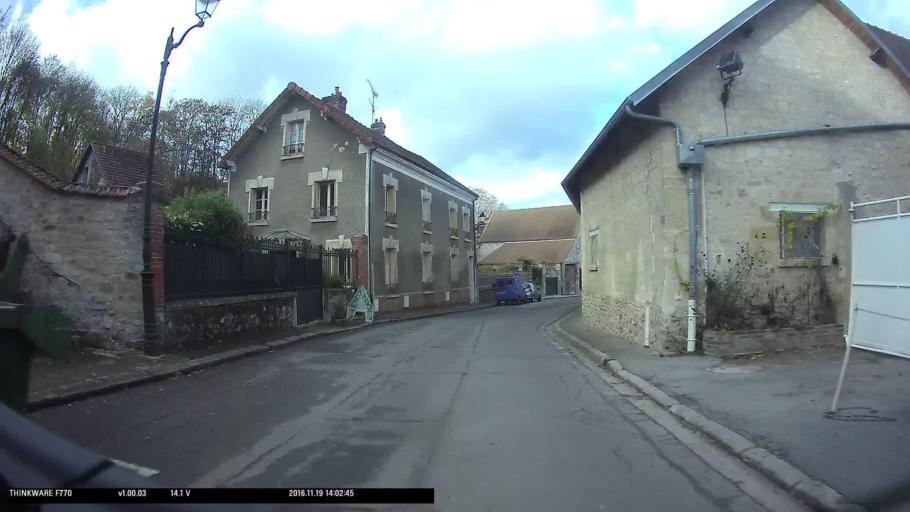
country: FR
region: Ile-de-France
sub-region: Departement du Val-d'Oise
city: Ableiges
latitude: 49.0761
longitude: 2.0041
